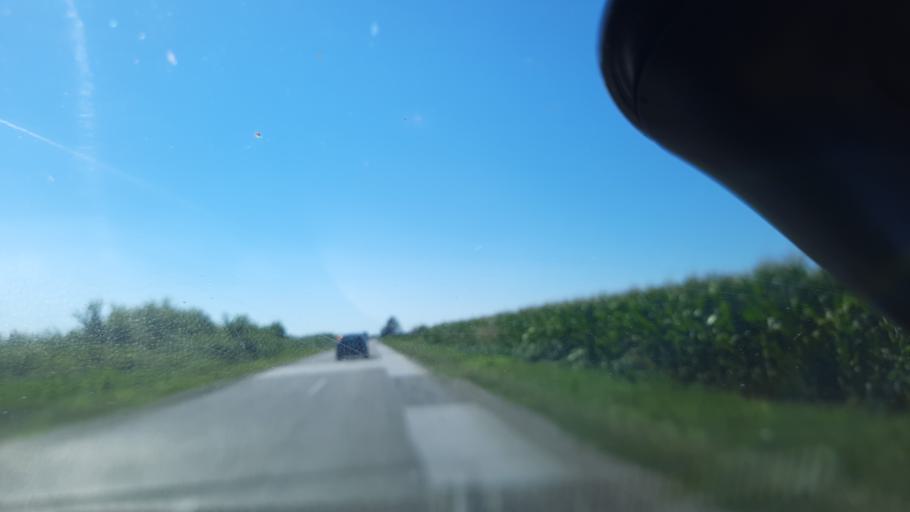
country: RS
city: Simanovci
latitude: 44.8823
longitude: 20.0365
